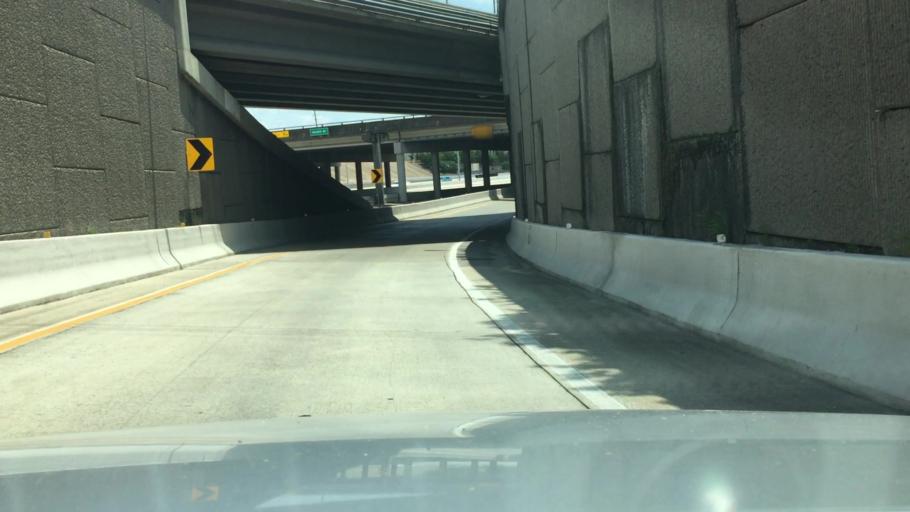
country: US
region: Texas
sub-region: Harris County
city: Bunker Hill Village
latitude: 29.7174
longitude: -95.5583
